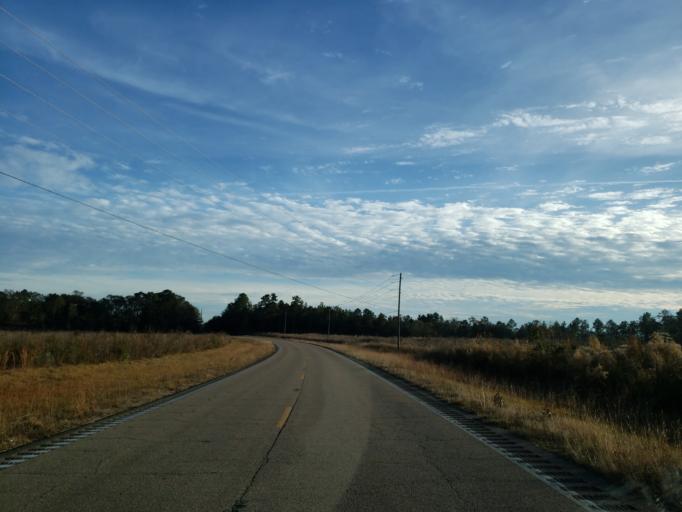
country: US
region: Mississippi
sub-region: Lamar County
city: West Hattiesburg
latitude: 31.2692
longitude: -89.4664
